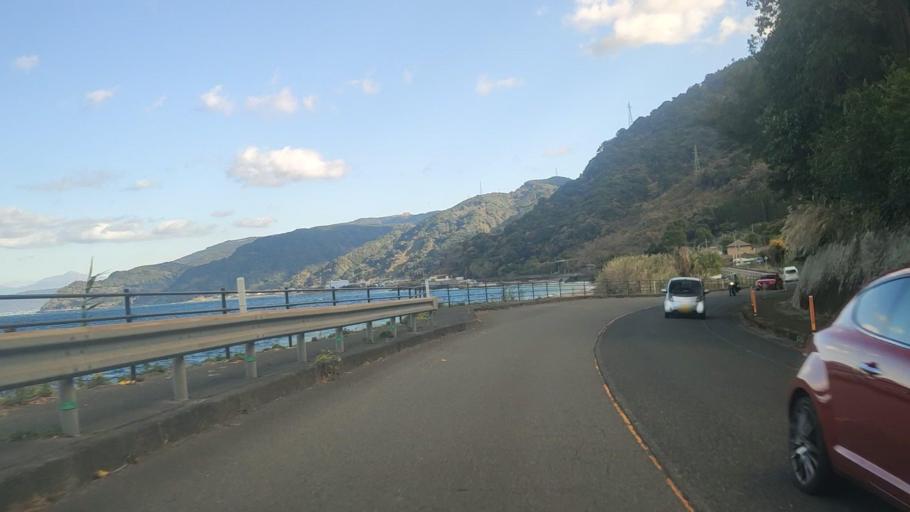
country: JP
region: Kagoshima
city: Tarumizu
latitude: 31.5702
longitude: 130.7729
